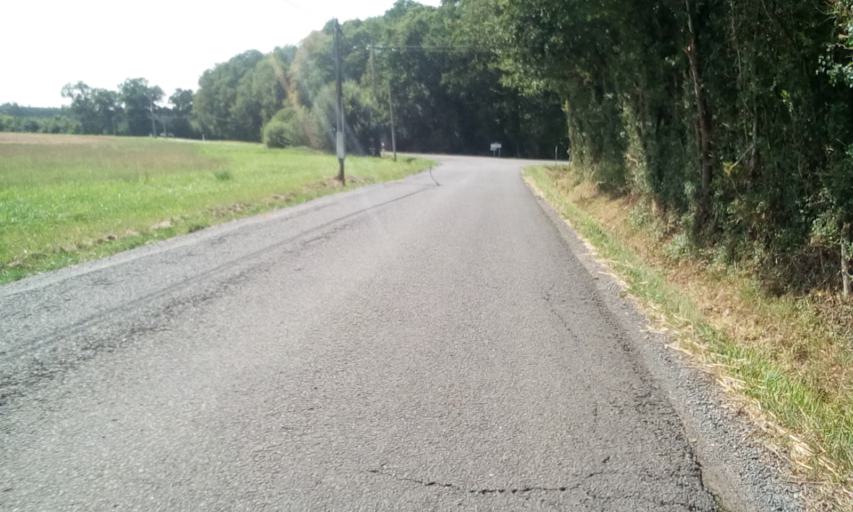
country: FR
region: Lower Normandy
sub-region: Departement du Calvados
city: Argences
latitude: 49.1539
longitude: -0.1332
